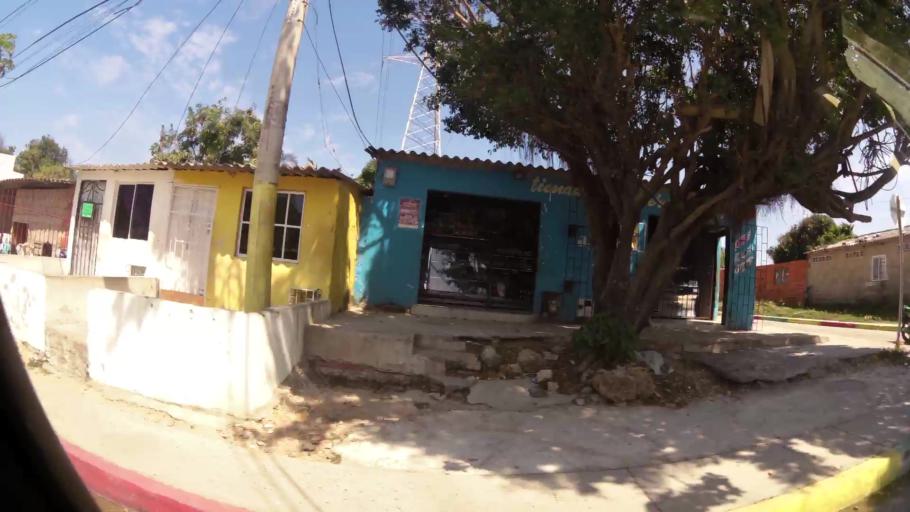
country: CO
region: Atlantico
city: Barranquilla
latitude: 10.9725
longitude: -74.8306
